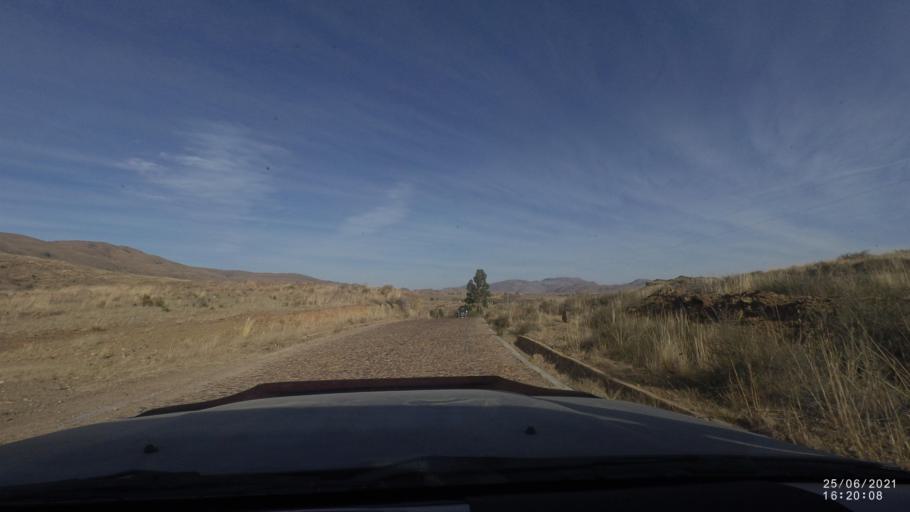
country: BO
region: Cochabamba
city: Cliza
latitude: -17.7445
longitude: -65.8419
